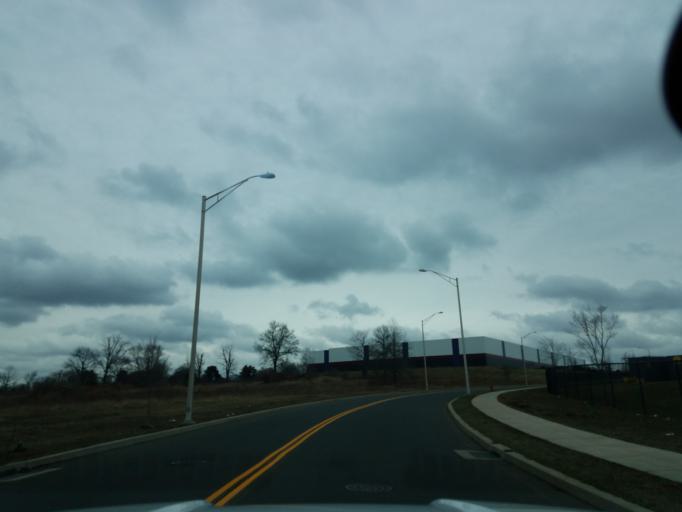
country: US
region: Connecticut
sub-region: Hartford County
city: Farmington
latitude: 41.6844
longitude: -72.8140
